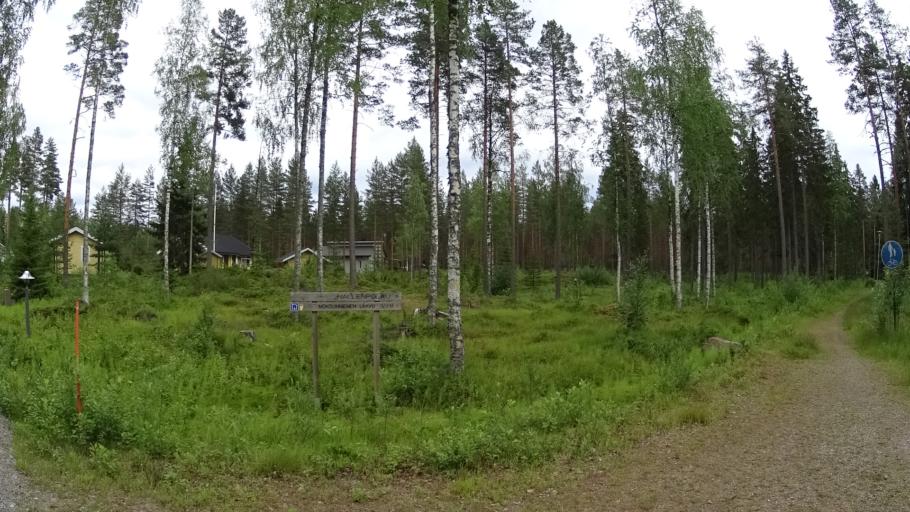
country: FI
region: Southern Ostrobothnia
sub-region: Kuusiokunnat
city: AEhtaeri
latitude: 62.5293
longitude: 24.1932
